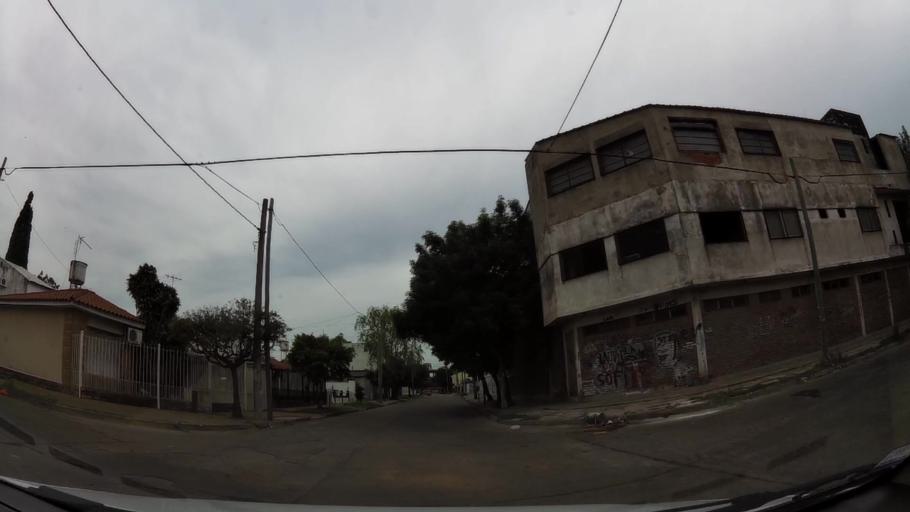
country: AR
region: Buenos Aires
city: San Justo
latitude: -34.6653
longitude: -58.5220
